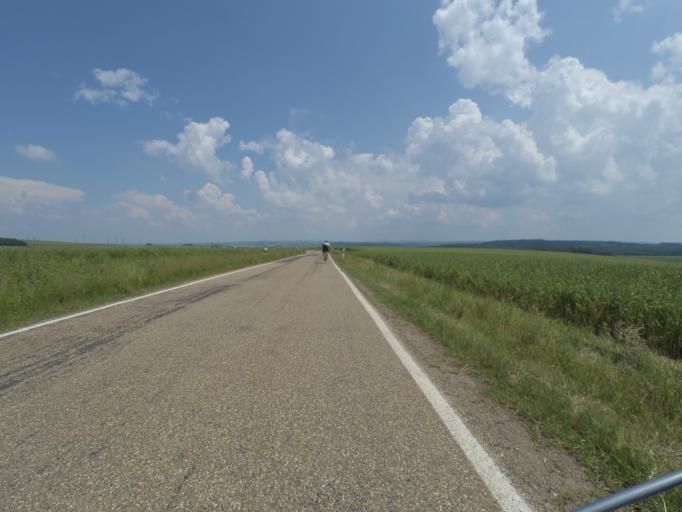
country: DE
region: Rheinland-Pfalz
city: Brohl
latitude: 50.2155
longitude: 7.2694
